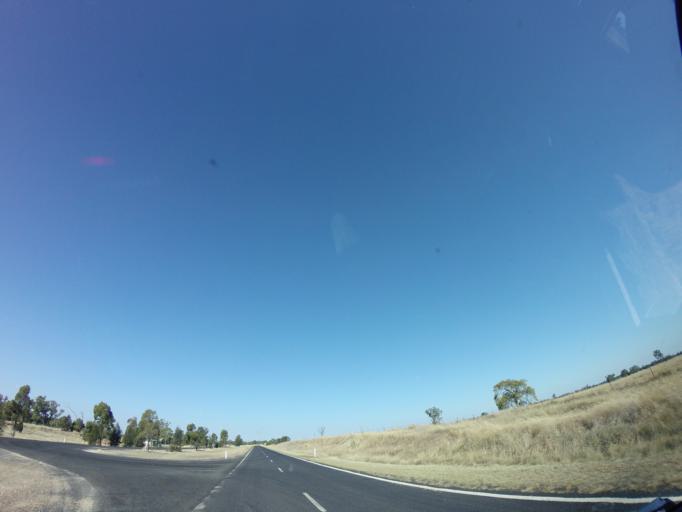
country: AU
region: New South Wales
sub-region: Gilgandra
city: Gilgandra
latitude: -31.6583
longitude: 148.4467
